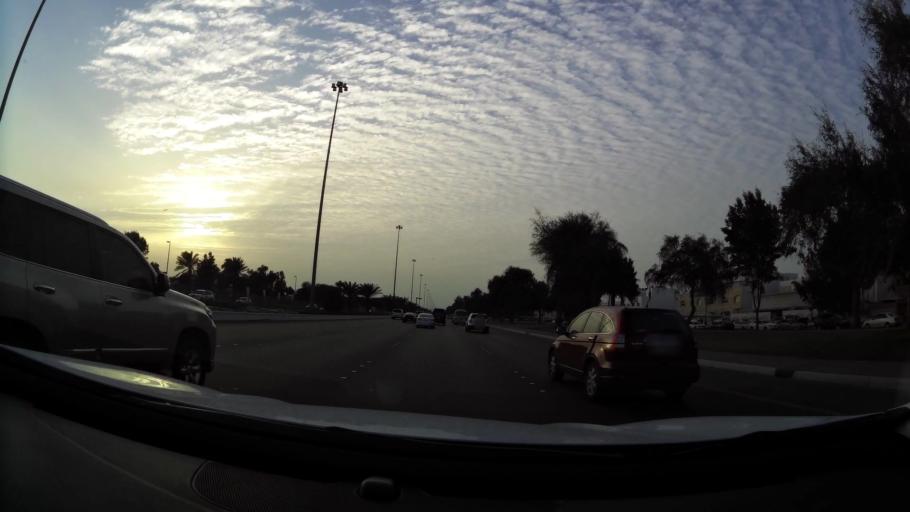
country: AE
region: Abu Dhabi
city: Abu Dhabi
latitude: 24.4259
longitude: 54.4057
